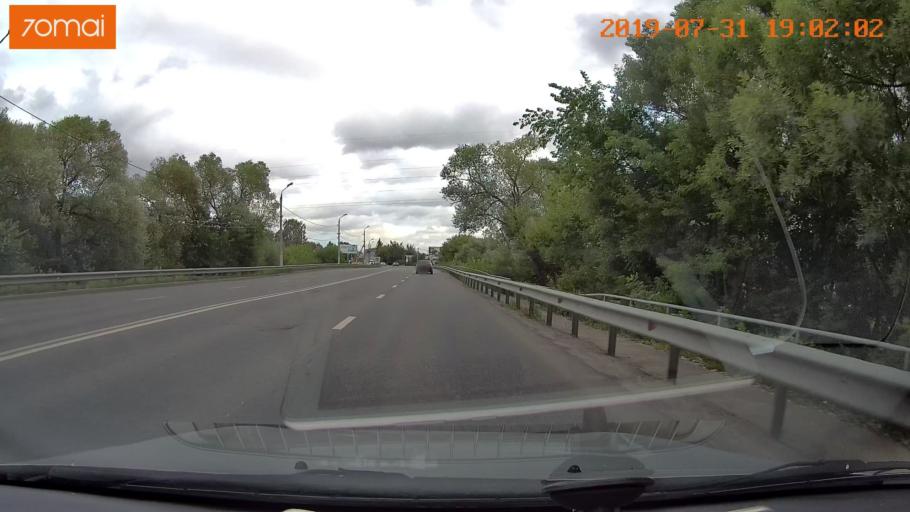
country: RU
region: Moskovskaya
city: Raduzhnyy
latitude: 55.1223
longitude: 38.7303
